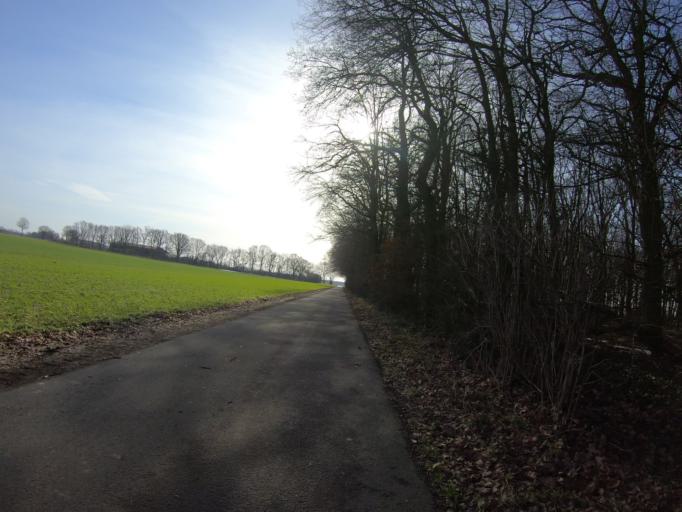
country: DE
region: Lower Saxony
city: Meine
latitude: 52.3994
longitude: 10.5597
